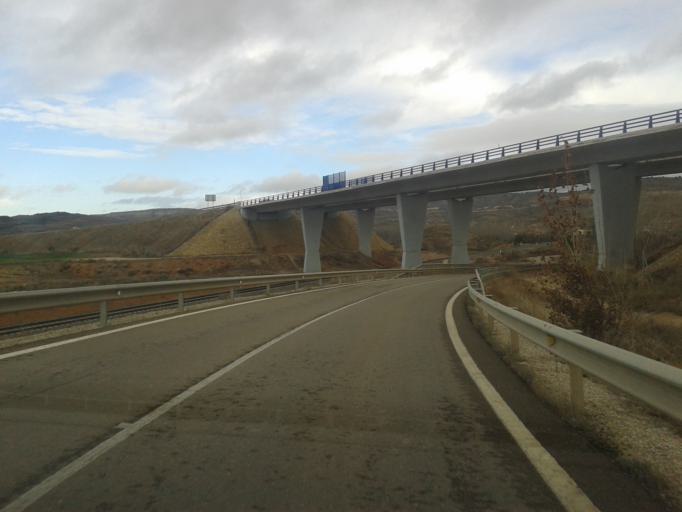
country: ES
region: Aragon
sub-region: Provincia de Teruel
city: Calamocha
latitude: 40.9251
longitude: -1.2674
